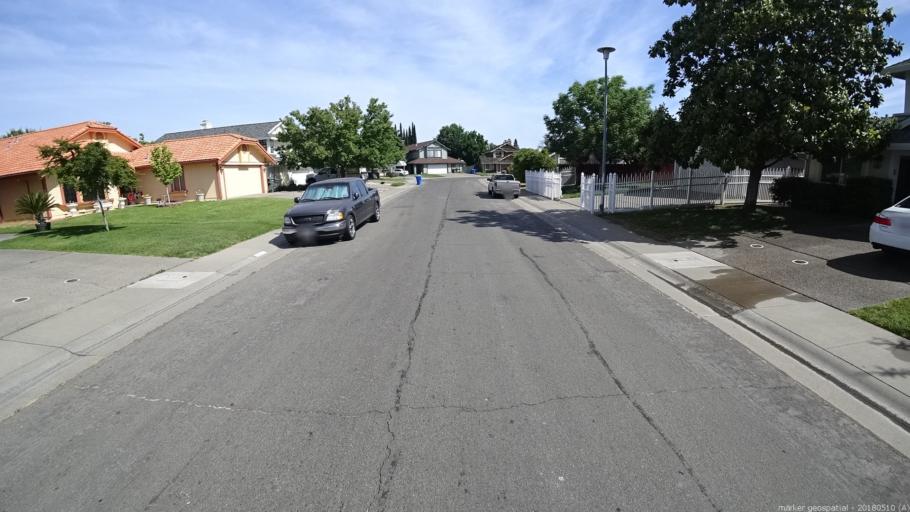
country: US
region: California
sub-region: Sacramento County
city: Rio Linda
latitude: 38.6575
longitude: -121.4627
